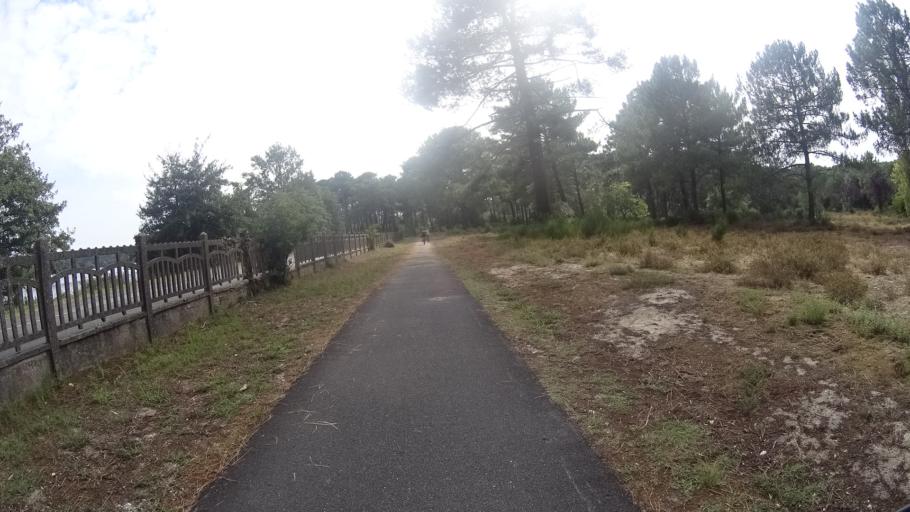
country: FR
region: Aquitaine
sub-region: Departement de la Gironde
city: Lacanau
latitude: 44.9985
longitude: -1.1411
